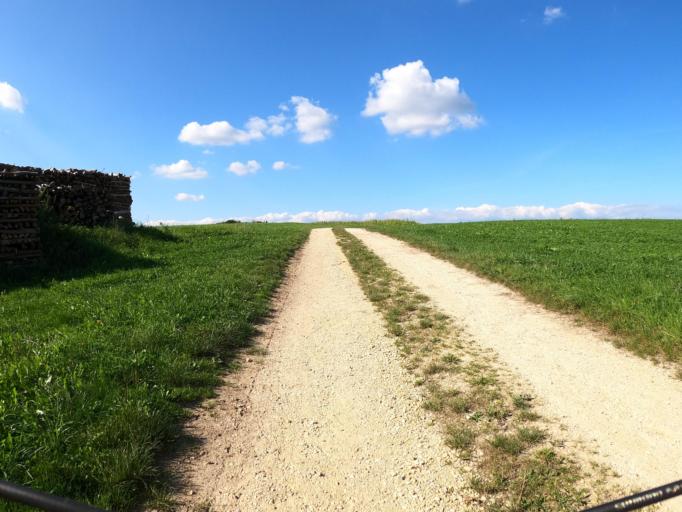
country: DE
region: Bavaria
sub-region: Swabia
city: Roggenburg
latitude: 48.3129
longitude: 10.2235
